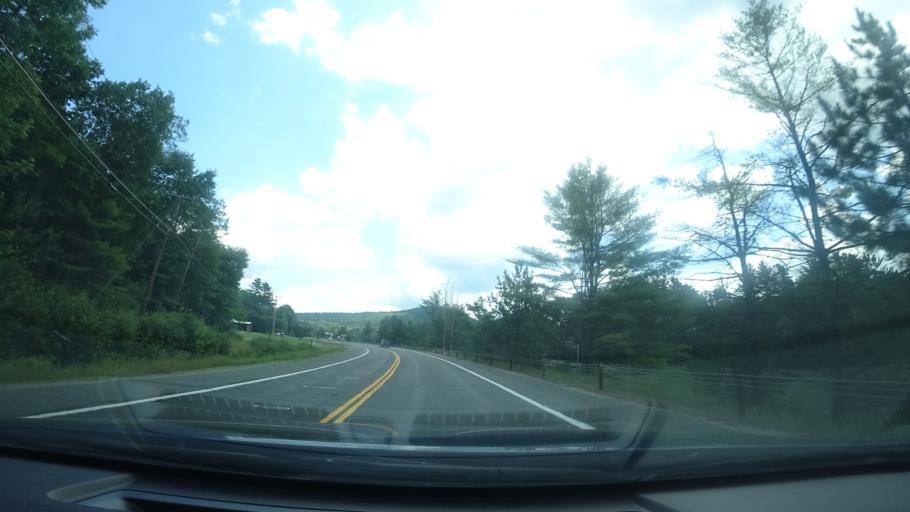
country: US
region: New York
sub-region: Warren County
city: Warrensburg
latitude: 43.6564
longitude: -73.8133
